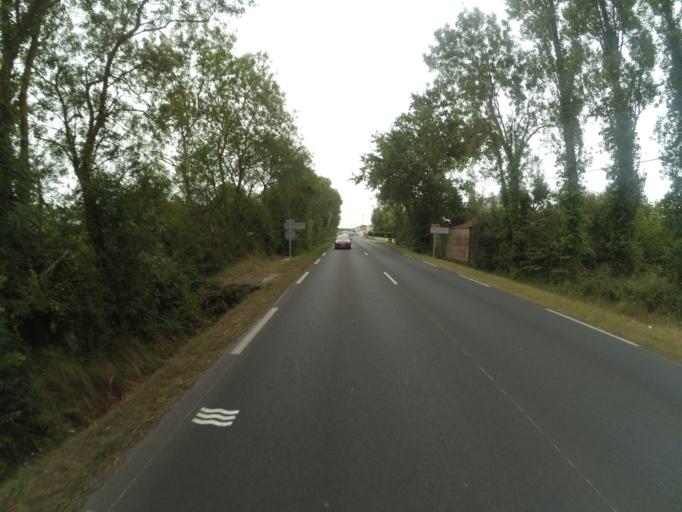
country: FR
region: Pays de la Loire
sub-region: Departement de la Vendee
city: Challans
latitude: 46.8595
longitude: -1.9072
